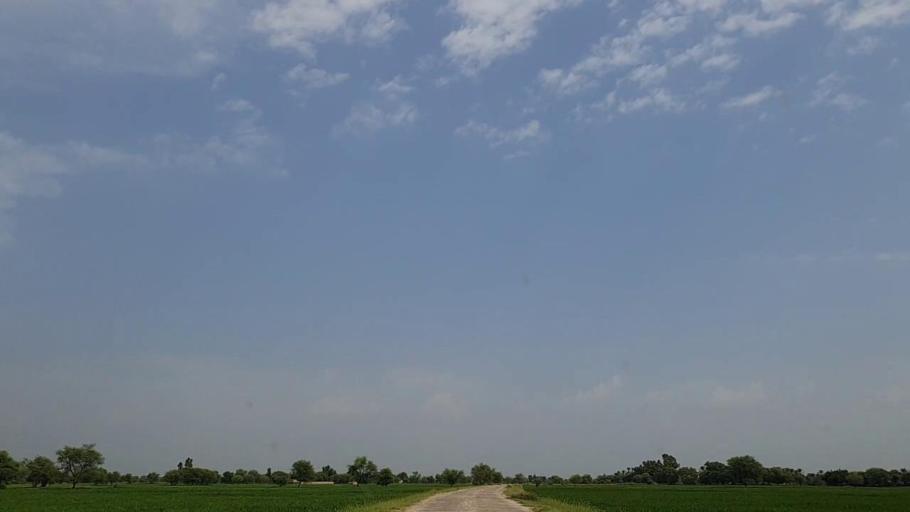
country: PK
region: Sindh
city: Khanpur
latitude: 27.8423
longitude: 69.4651
